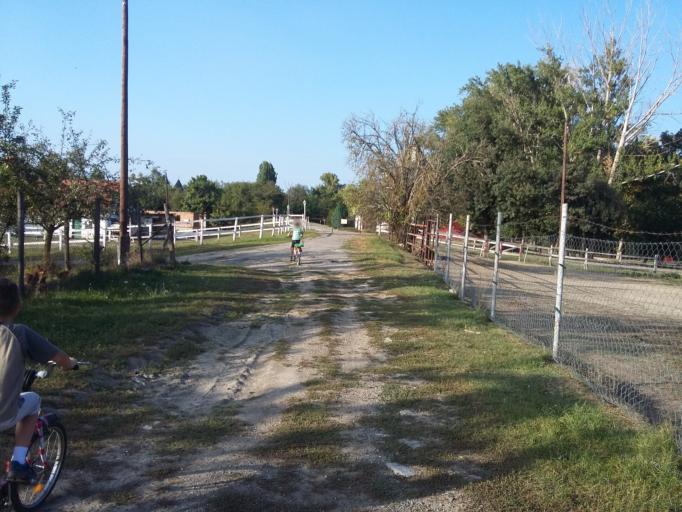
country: HU
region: Csongrad
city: Szeged
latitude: 46.2043
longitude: 20.1142
